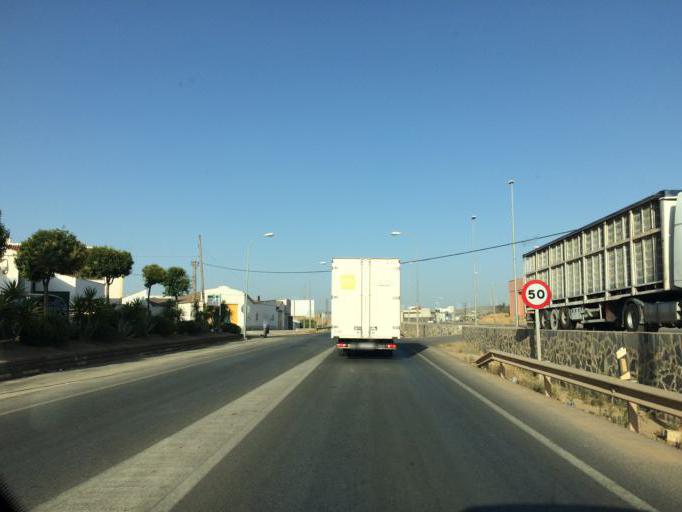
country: ES
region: Andalusia
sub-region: Provincia de Malaga
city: Campillos
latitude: 37.0529
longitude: -4.8646
